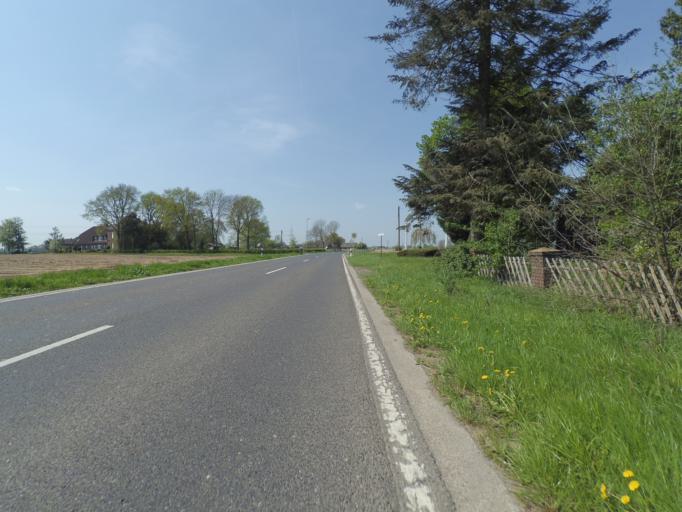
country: DE
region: North Rhine-Westphalia
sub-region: Regierungsbezirk Munster
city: Isselburg
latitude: 51.8127
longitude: 6.4327
